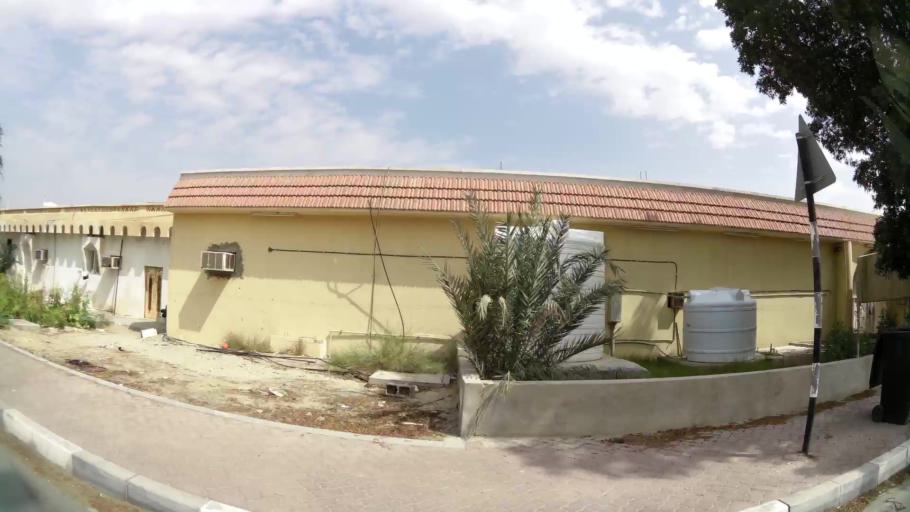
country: AE
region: Abu Dhabi
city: Abu Dhabi
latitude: 24.3007
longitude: 54.6232
